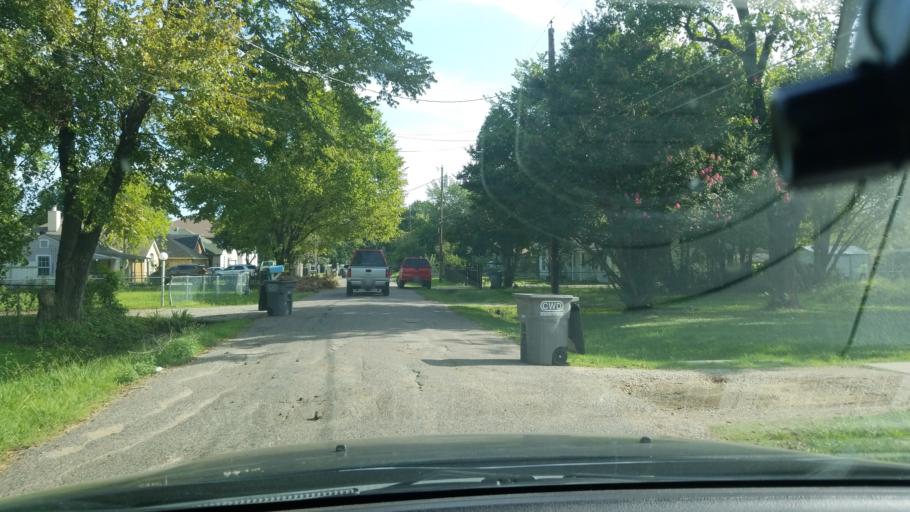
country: US
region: Texas
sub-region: Dallas County
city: Balch Springs
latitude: 32.7144
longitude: -96.6330
